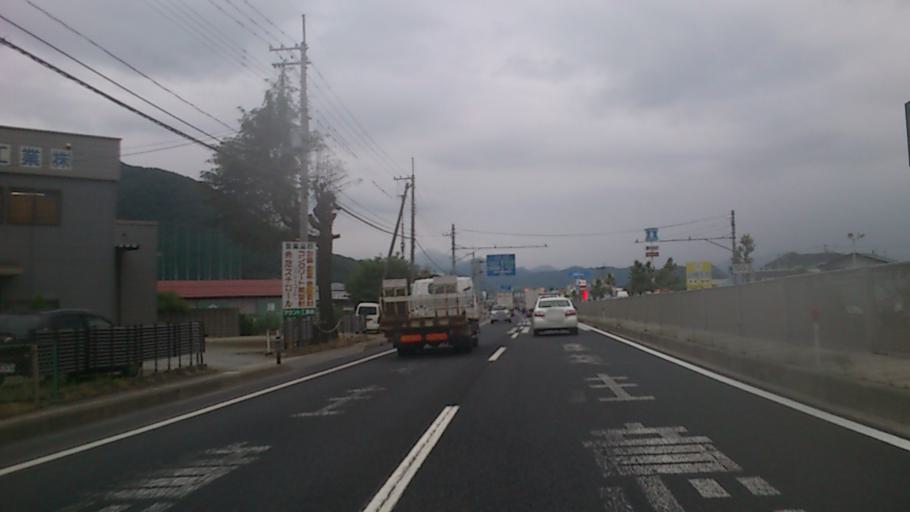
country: JP
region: Yamagata
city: Tendo
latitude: 38.3684
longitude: 140.3850
